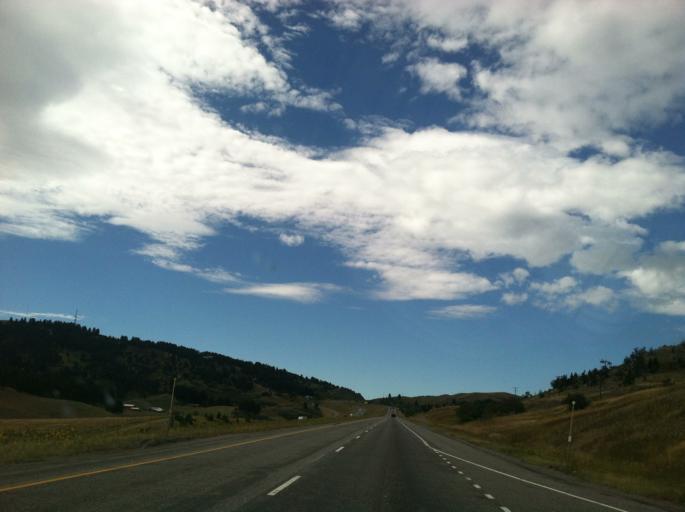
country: US
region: Montana
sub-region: Park County
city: Livingston
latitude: 45.6587
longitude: -110.7826
